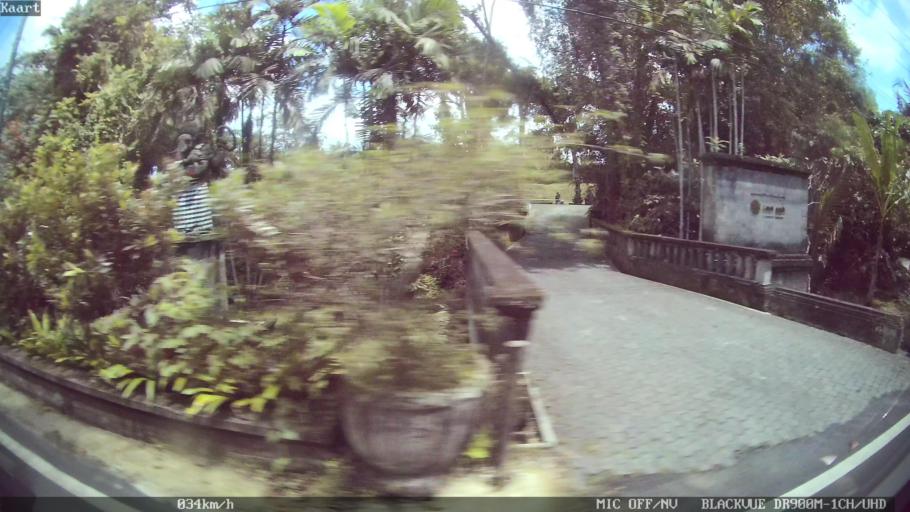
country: ID
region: Bali
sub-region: Kabupaten Gianyar
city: Ubud
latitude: -8.5233
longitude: 115.2831
